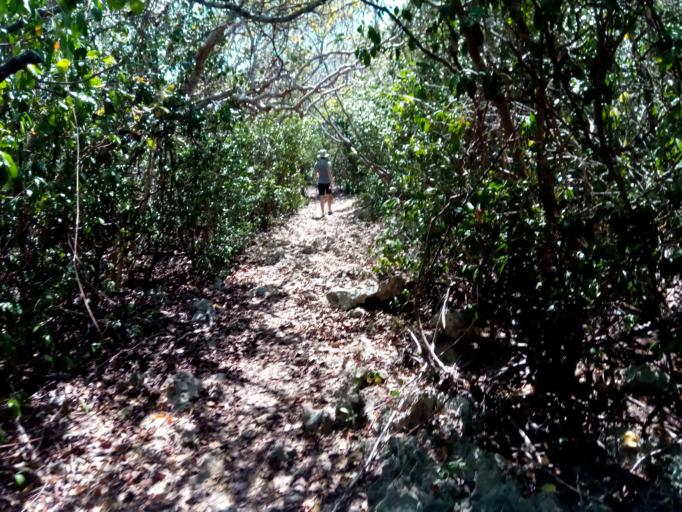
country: GP
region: Guadeloupe
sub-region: Guadeloupe
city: Saint-Francois
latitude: 16.2662
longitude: -61.2331
